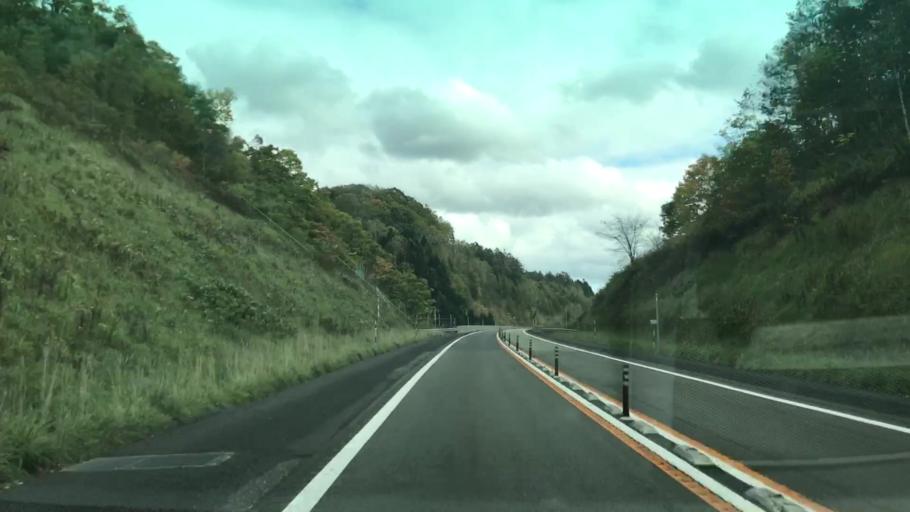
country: JP
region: Hokkaido
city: Chitose
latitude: 42.9147
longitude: 141.9706
